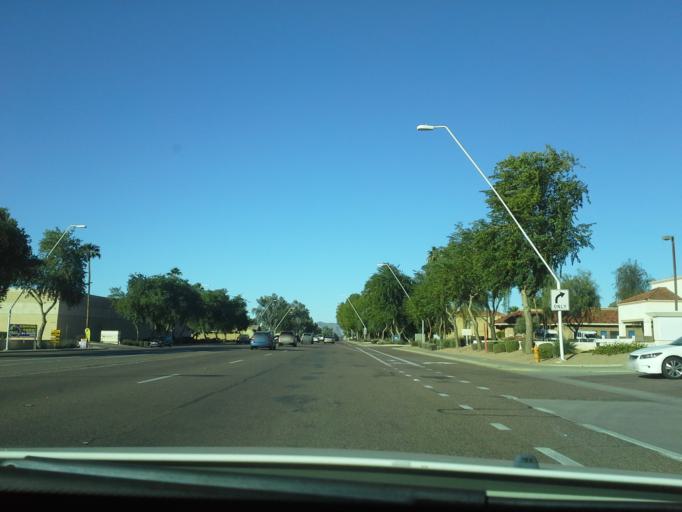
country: US
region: Arizona
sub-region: Maricopa County
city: San Carlos
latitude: 33.3498
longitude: -111.8597
